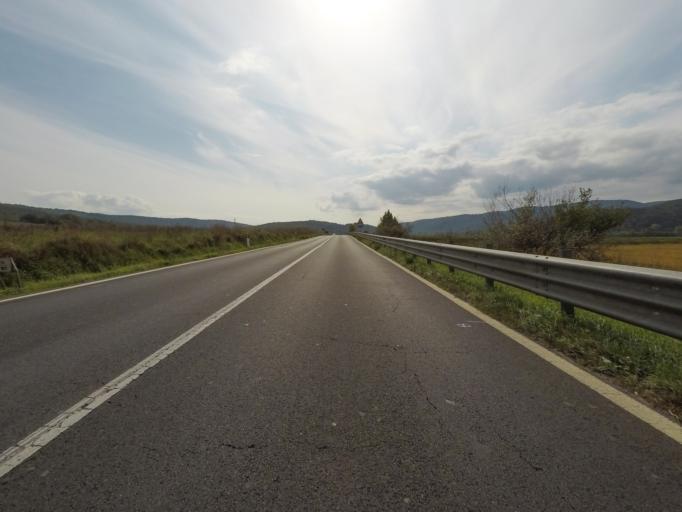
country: IT
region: Tuscany
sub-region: Provincia di Siena
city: Murlo
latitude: 43.1656
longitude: 11.2872
